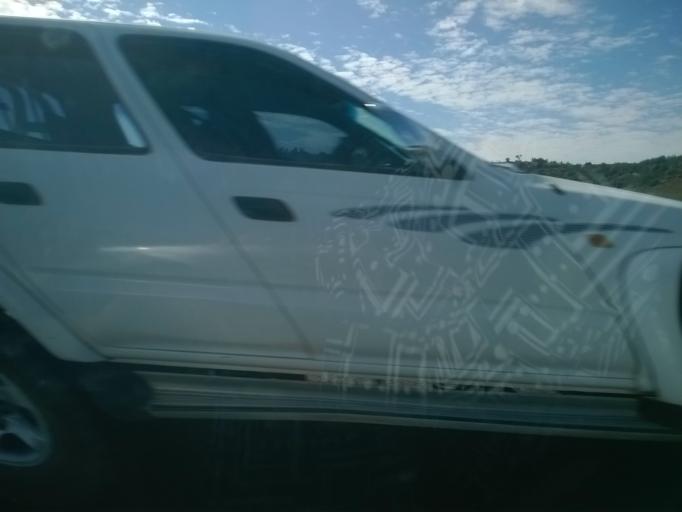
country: LS
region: Leribe
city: Maputsoe
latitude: -29.0872
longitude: 27.9480
